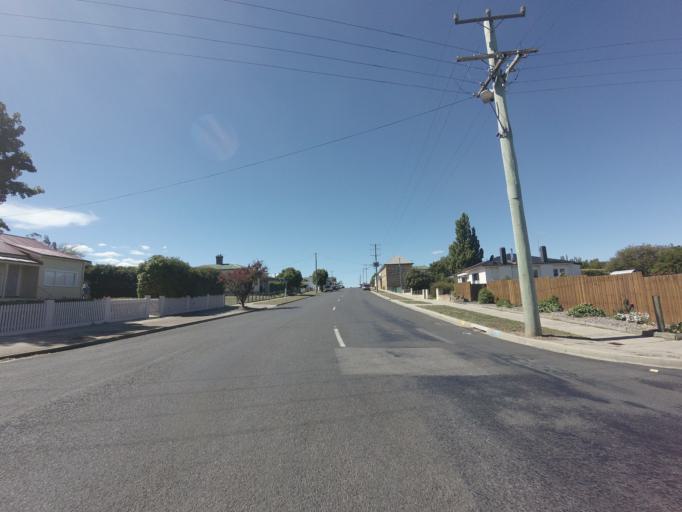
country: AU
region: Tasmania
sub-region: Northern Midlands
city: Evandale
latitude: -41.7822
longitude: 147.7204
